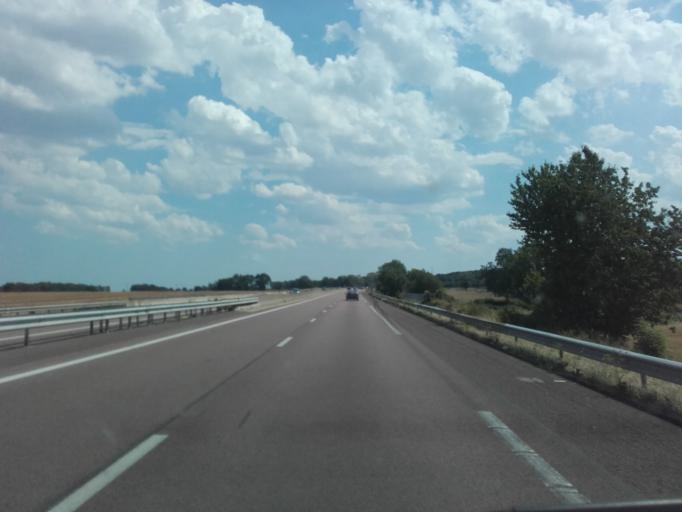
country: FR
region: Bourgogne
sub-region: Departement de l'Yonne
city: Avallon
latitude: 47.5321
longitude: 3.9813
